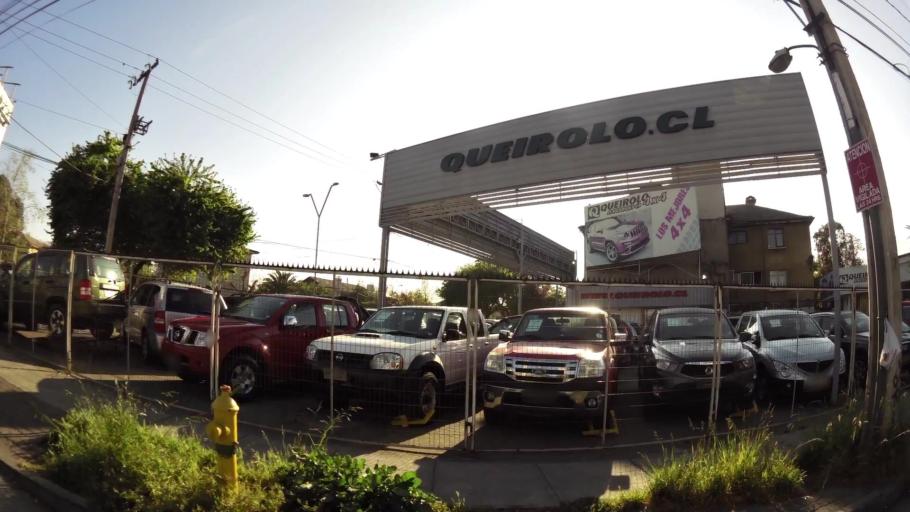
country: CL
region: Santiago Metropolitan
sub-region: Provincia de Santiago
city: Villa Presidente Frei, Nunoa, Santiago, Chile
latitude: -33.4319
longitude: -70.5838
